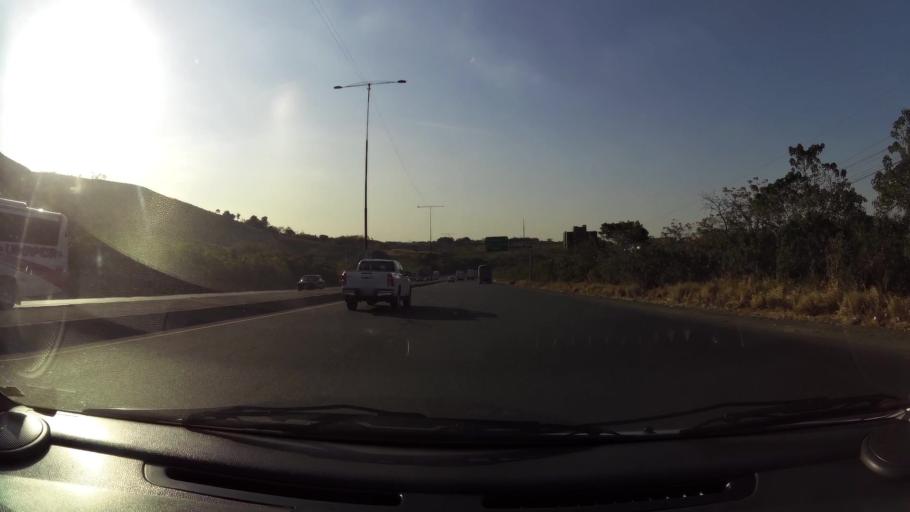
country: EC
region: Guayas
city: Santa Lucia
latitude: -2.1621
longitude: -79.9487
